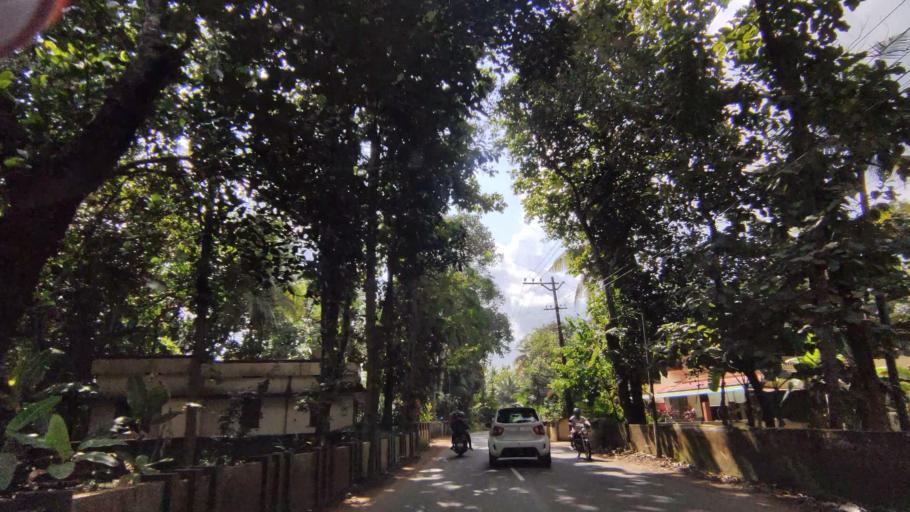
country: IN
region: Kerala
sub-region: Kottayam
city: Kottayam
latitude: 9.6883
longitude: 76.5013
